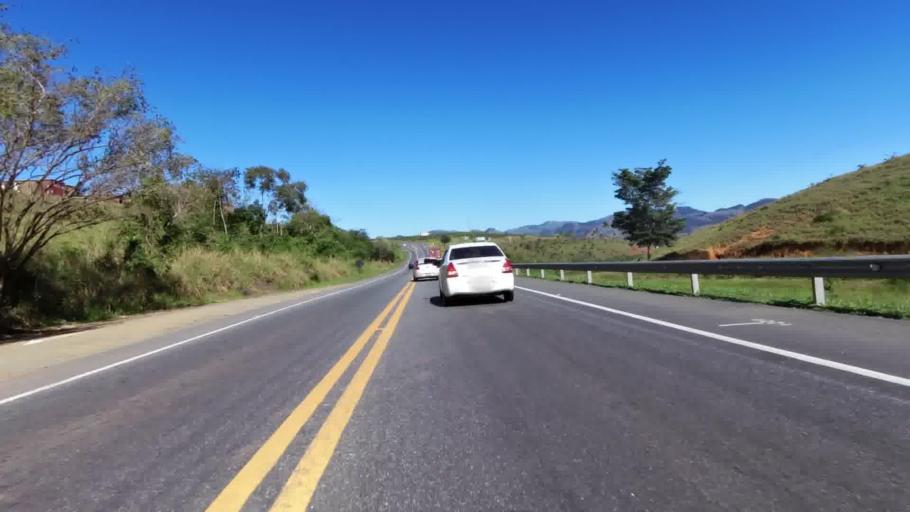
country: BR
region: Espirito Santo
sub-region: Alfredo Chaves
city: Alfredo Chaves
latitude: -20.6893
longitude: -40.6971
